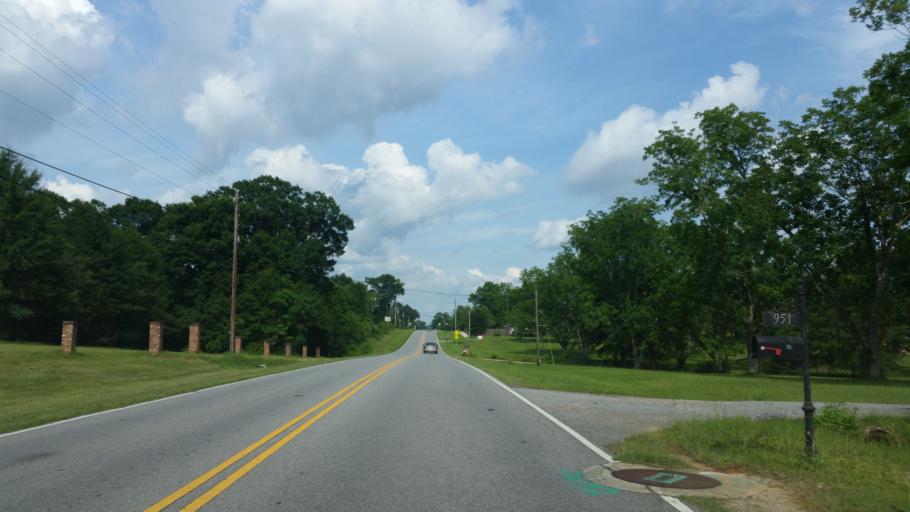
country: US
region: Florida
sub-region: Escambia County
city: Gonzalez
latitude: 30.5704
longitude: -87.3027
